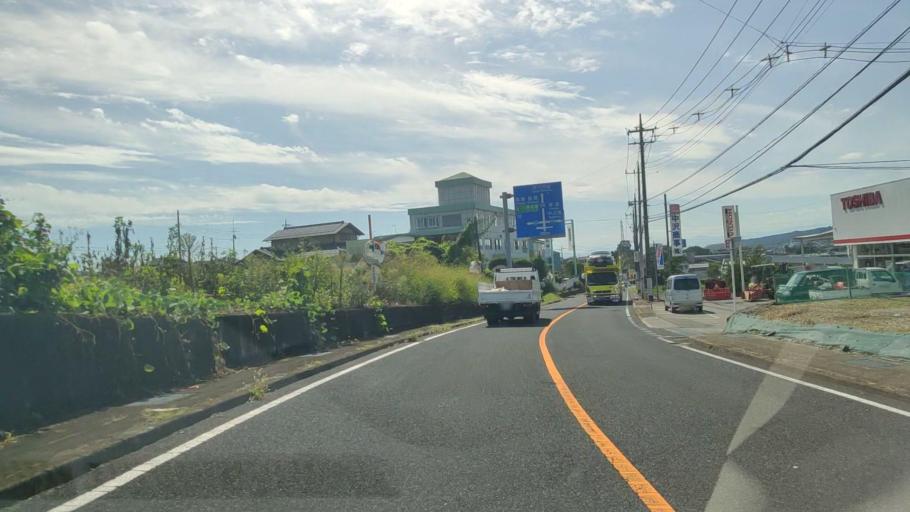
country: JP
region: Gunma
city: Shibukawa
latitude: 36.5234
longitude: 139.0115
